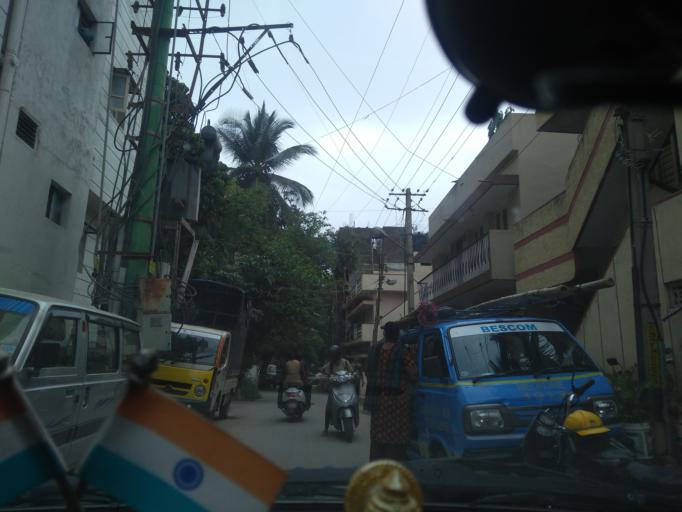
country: IN
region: Karnataka
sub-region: Bangalore Urban
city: Bangalore
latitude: 13.0074
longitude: 77.5565
